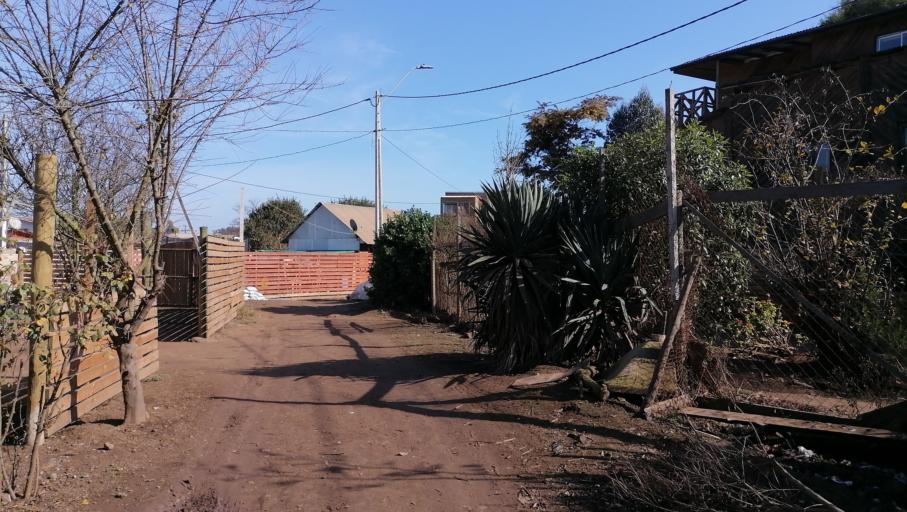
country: CL
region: Valparaiso
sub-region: Provincia de Valparaiso
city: Vina del Mar
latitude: -32.9007
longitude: -71.4944
